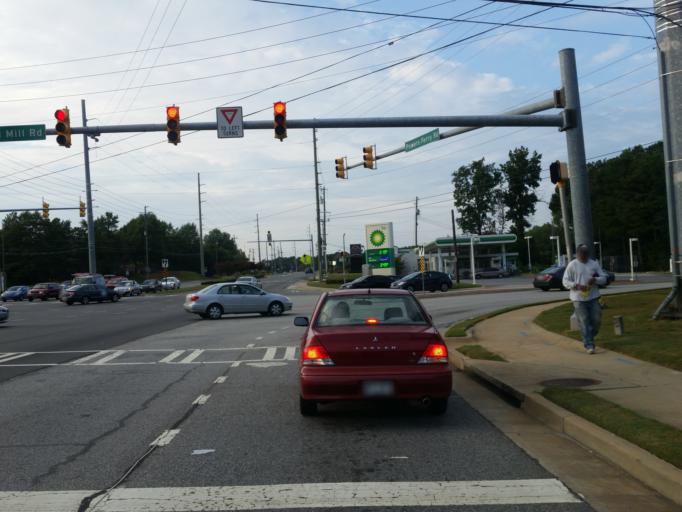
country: US
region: Georgia
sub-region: Cobb County
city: Vinings
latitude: 33.9178
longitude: -84.4666
